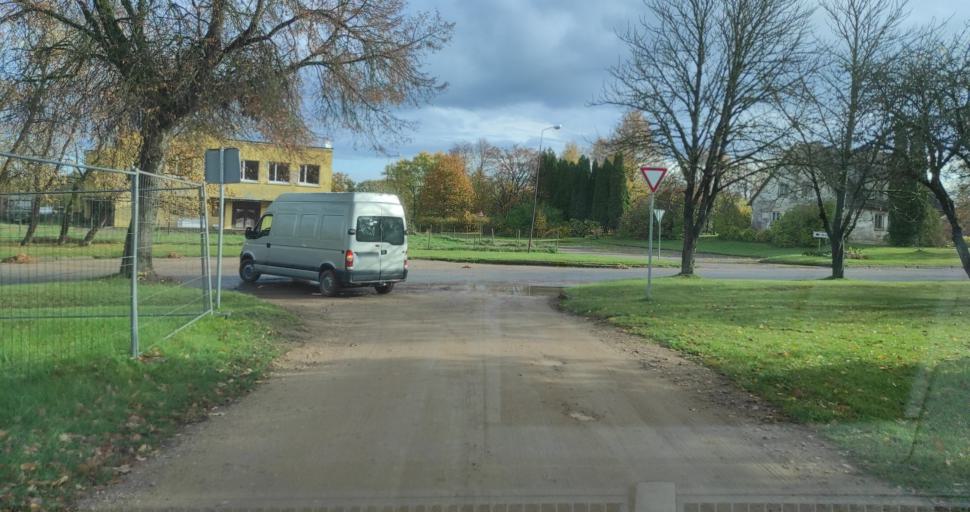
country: LV
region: Vainode
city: Vainode
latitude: 56.5706
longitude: 21.8973
